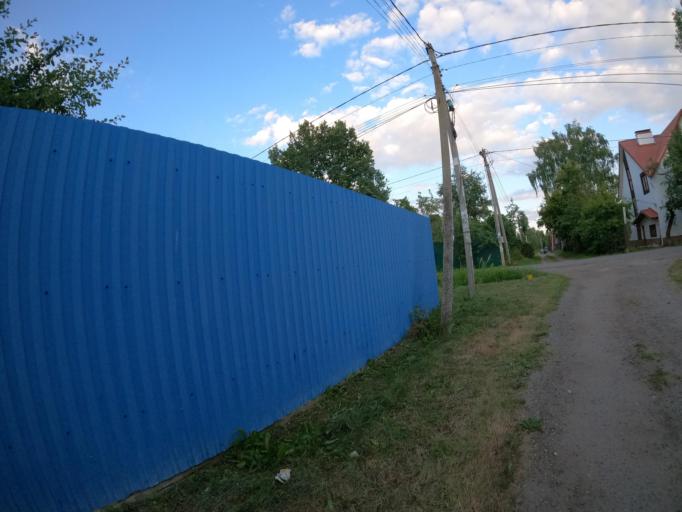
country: RU
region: Moskovskaya
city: Ashitkovo
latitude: 55.4306
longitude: 38.5674
